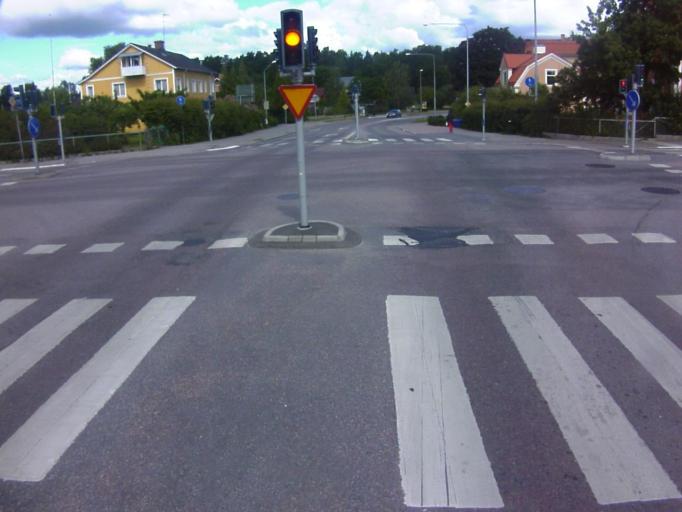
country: SE
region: Soedermanland
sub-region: Eskilstuna Kommun
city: Eskilstuna
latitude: 59.3607
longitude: 16.4980
